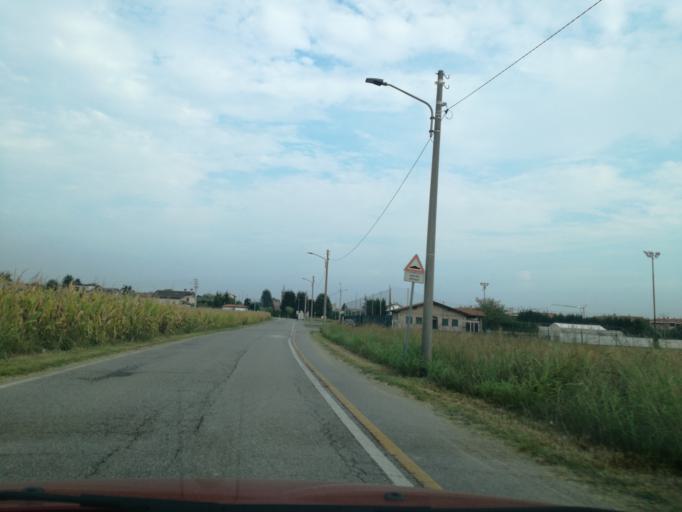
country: IT
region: Lombardy
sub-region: Provincia di Monza e Brianza
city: Villanova
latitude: 45.6417
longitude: 9.3854
